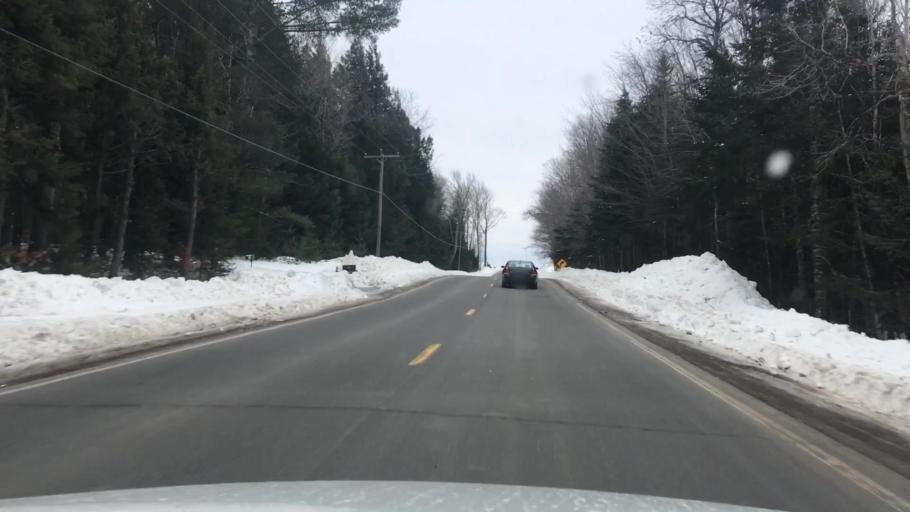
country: US
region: Maine
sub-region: Penobscot County
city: Garland
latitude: 44.9851
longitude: -69.0877
